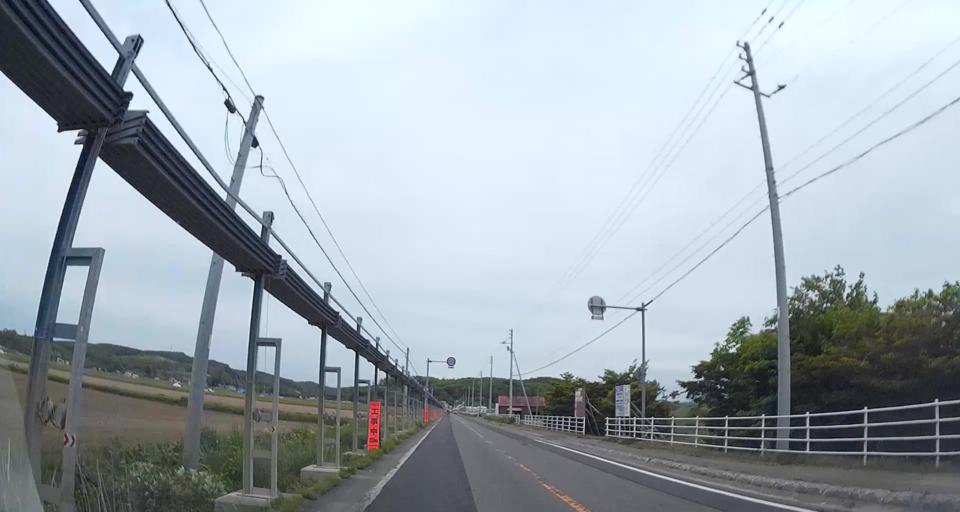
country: JP
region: Hokkaido
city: Chitose
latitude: 42.7324
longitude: 141.8877
